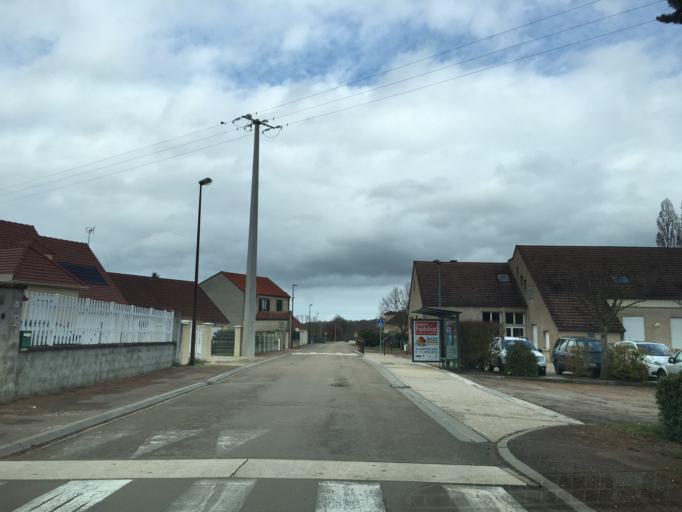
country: FR
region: Bourgogne
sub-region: Departement de l'Yonne
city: Charbuy
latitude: 47.8304
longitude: 3.4593
